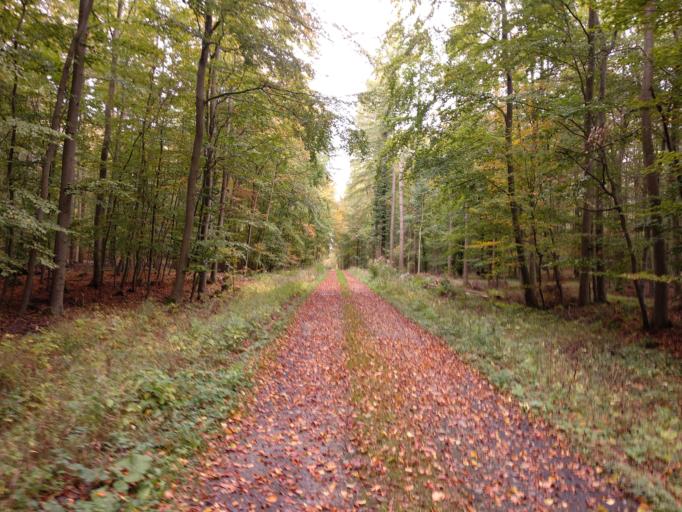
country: DE
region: North Rhine-Westphalia
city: Beverungen
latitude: 51.6638
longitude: 9.3359
